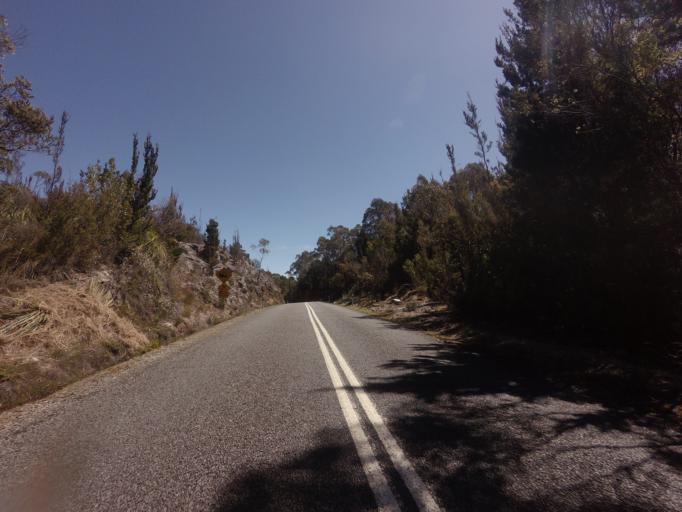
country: AU
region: Tasmania
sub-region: Huon Valley
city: Geeveston
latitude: -42.8140
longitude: 146.3793
